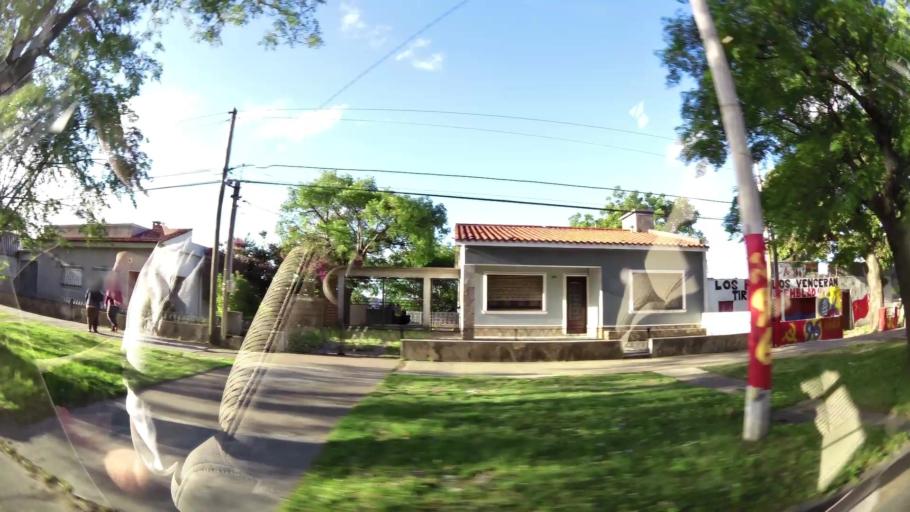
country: UY
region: Montevideo
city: Montevideo
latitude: -34.8757
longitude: -56.2628
